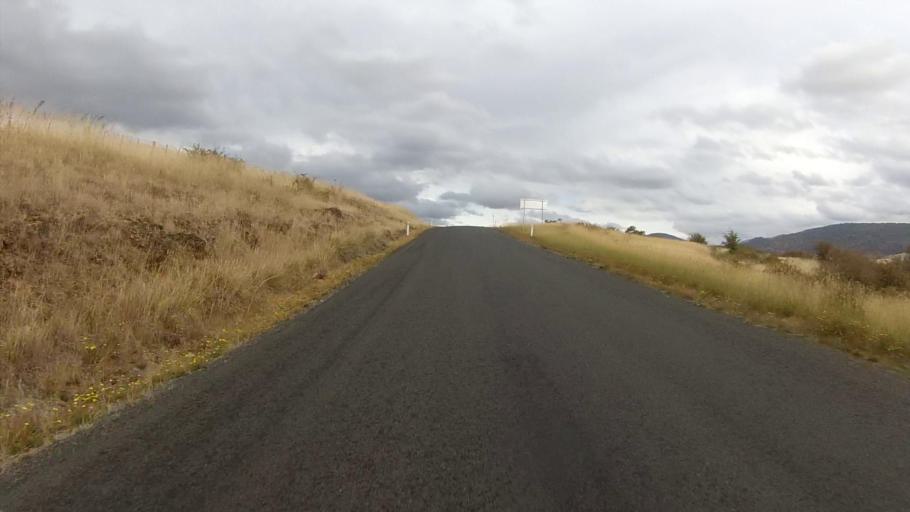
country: AU
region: Tasmania
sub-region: Northern Midlands
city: Evandale
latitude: -41.8174
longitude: 147.7540
